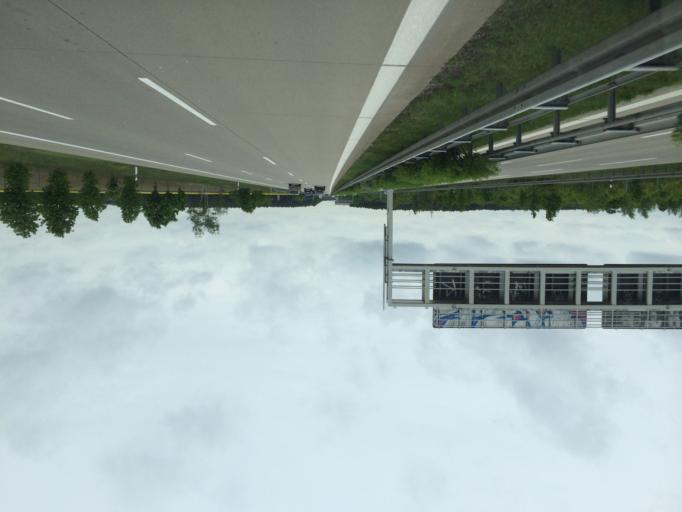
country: DE
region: Brandenburg
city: Wollin
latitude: 52.2924
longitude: 12.4621
